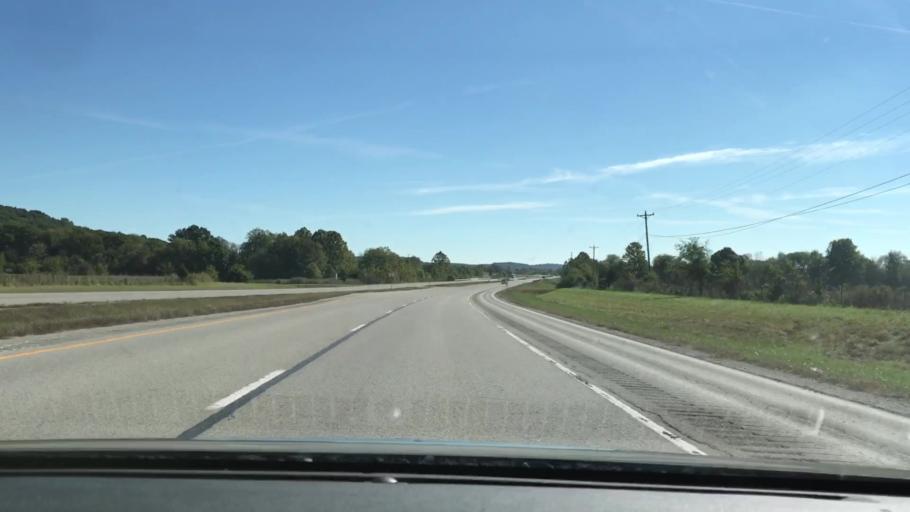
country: US
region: Kentucky
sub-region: Todd County
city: Elkton
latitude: 36.8455
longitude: -87.2774
